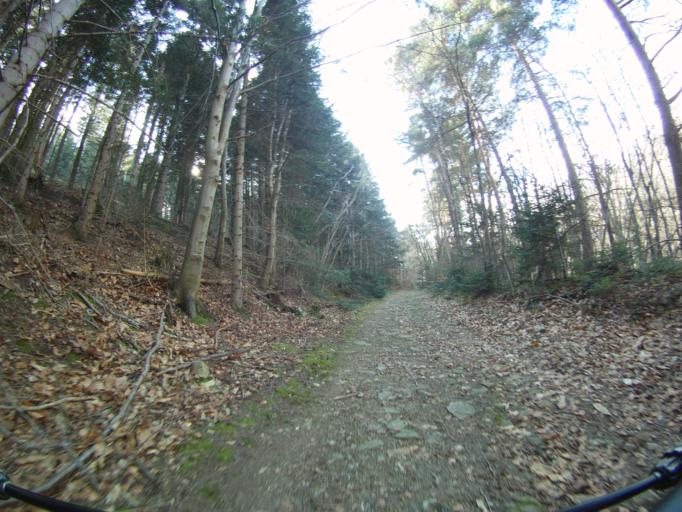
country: FR
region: Auvergne
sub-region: Departement du Puy-de-Dome
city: Ceyrat
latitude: 45.7331
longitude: 3.0521
